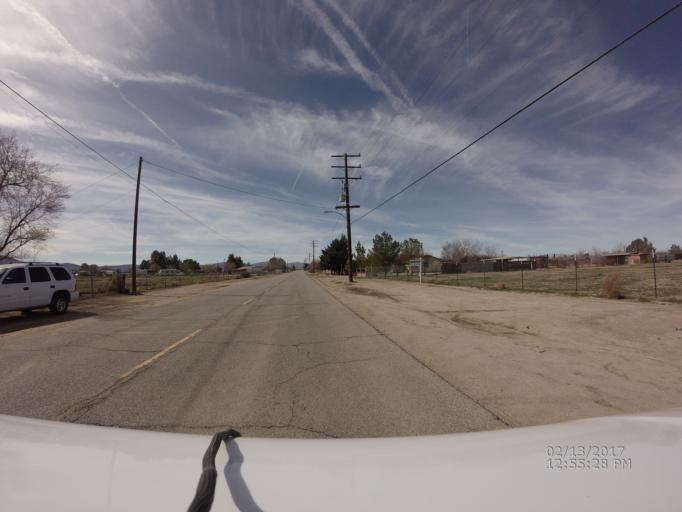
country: US
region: California
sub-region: Los Angeles County
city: Littlerock
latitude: 34.5724
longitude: -117.9631
